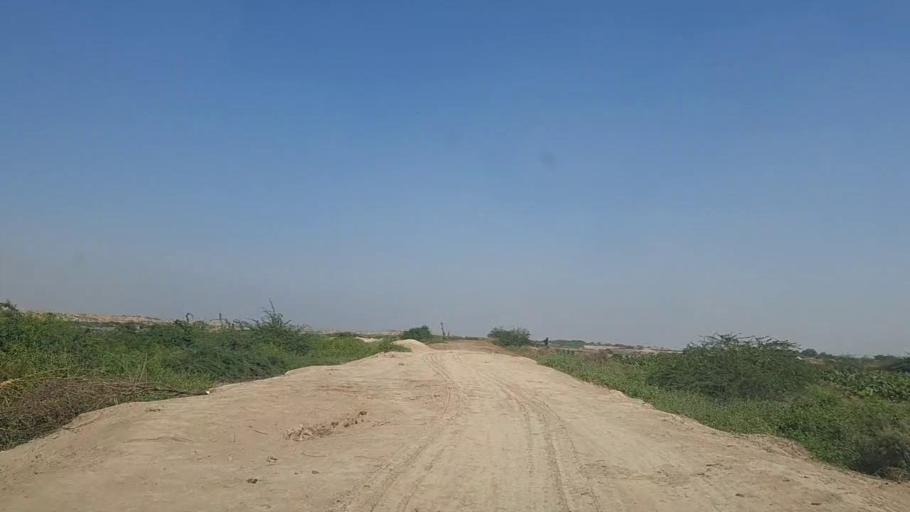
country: PK
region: Sindh
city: Thatta
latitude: 24.8420
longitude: 68.0220
